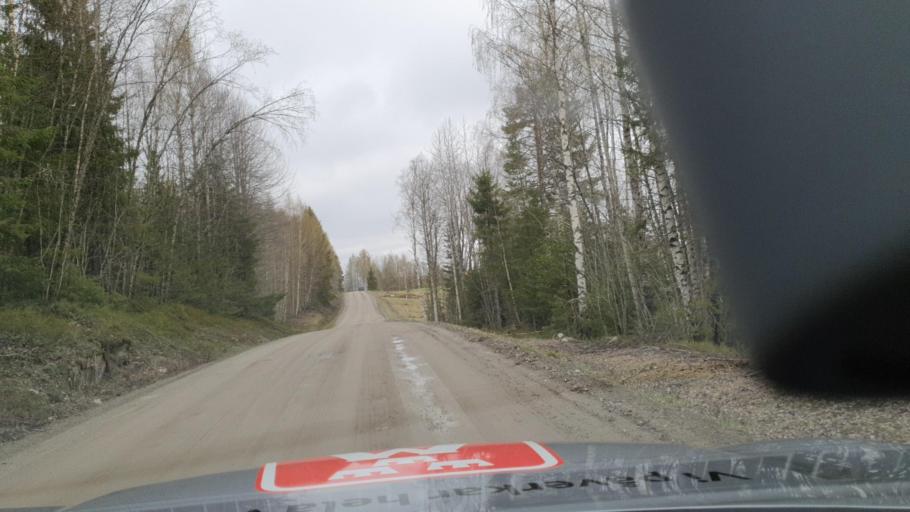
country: SE
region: Vaesternorrland
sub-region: OErnskoeldsviks Kommun
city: Husum
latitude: 63.6356
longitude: 19.0587
